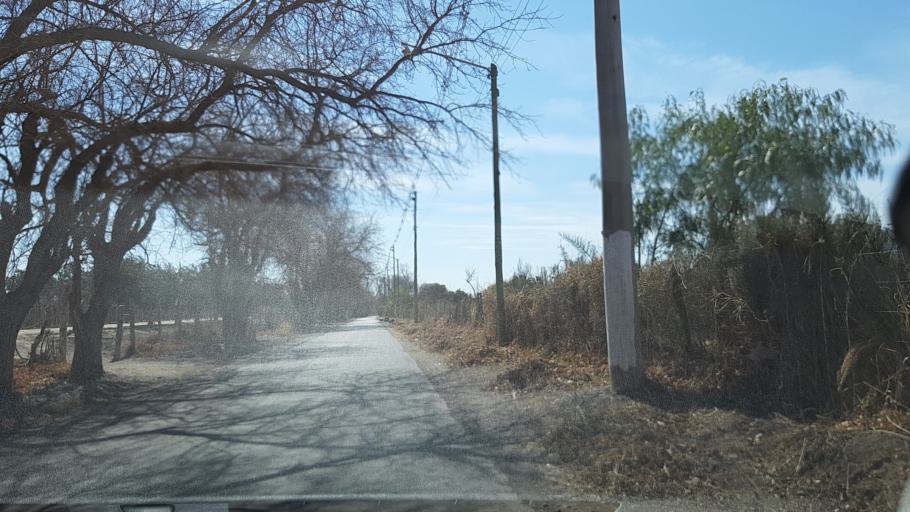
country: AR
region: San Juan
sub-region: Departamento de Zonda
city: Zonda
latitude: -31.5643
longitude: -68.7300
